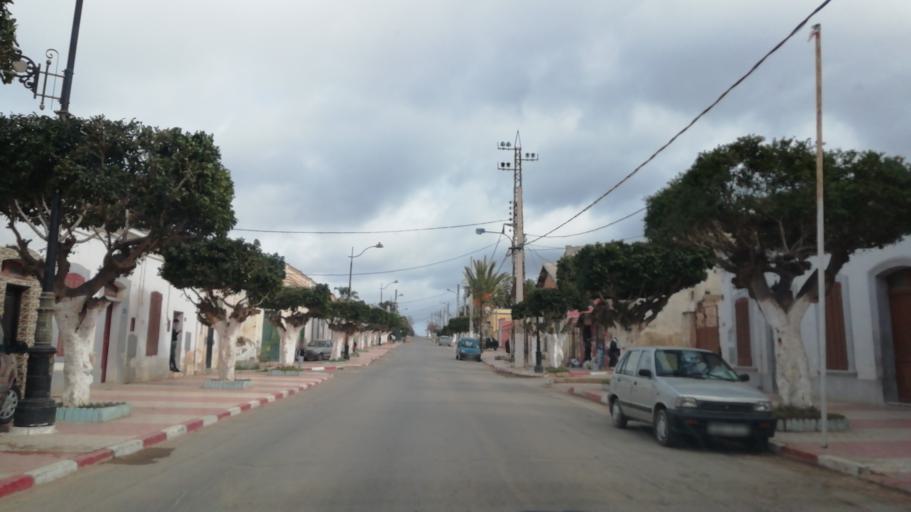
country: DZ
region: Oran
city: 'Ain el Turk
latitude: 35.6869
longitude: -0.8682
